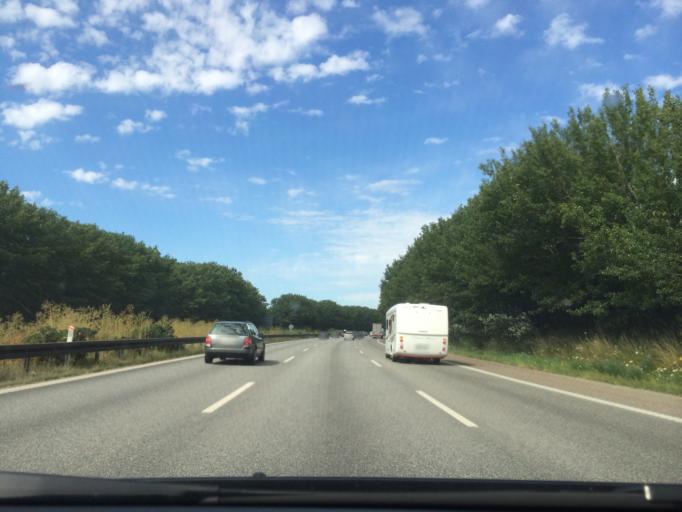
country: DK
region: Capital Region
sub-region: Hvidovre Kommune
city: Hvidovre
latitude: 55.6155
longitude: 12.4610
